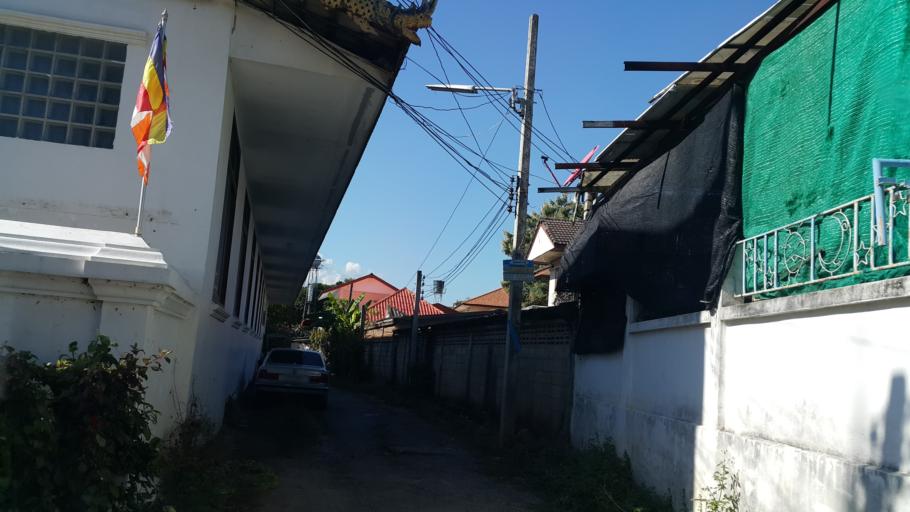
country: TH
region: Chiang Mai
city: Chiang Mai
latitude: 18.7630
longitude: 98.9974
